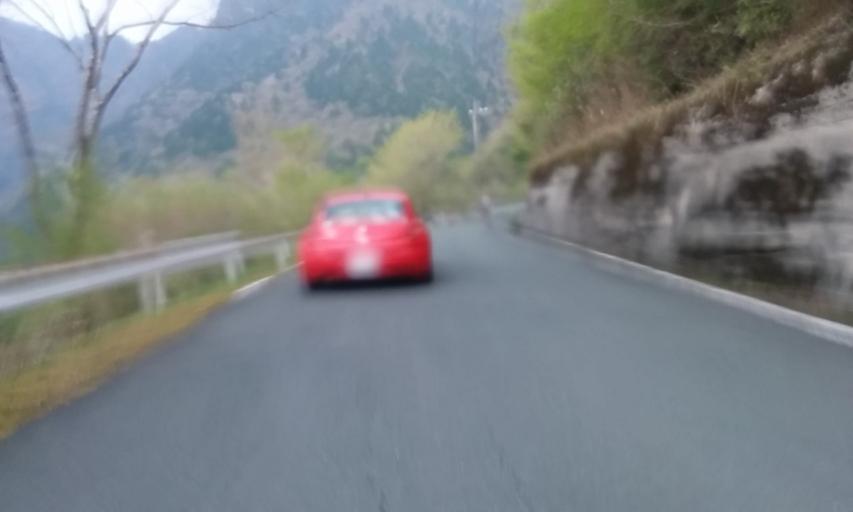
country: JP
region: Ehime
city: Saijo
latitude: 33.8009
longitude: 133.2686
